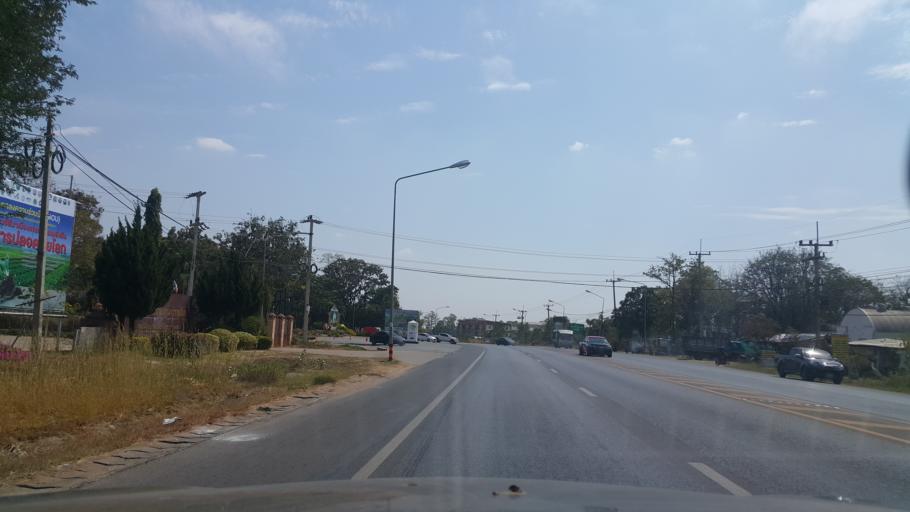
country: TH
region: Nakhon Ratchasima
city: Nakhon Ratchasima
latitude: 14.8505
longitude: 102.0736
